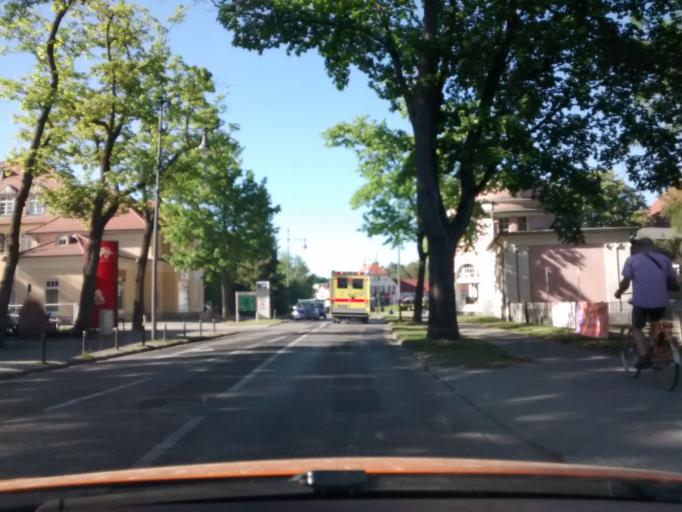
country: DE
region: Brandenburg
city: Bad Saarow
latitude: 52.2921
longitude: 14.0635
